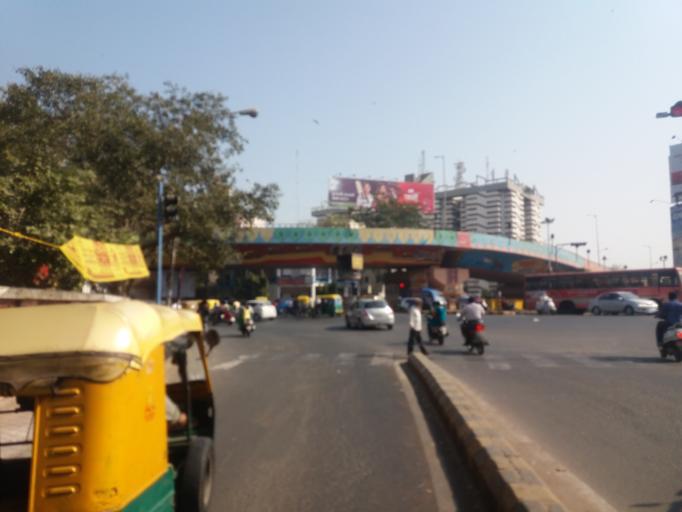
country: IN
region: Gujarat
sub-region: Ahmadabad
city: Ahmedabad
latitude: 23.0224
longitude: 72.5709
